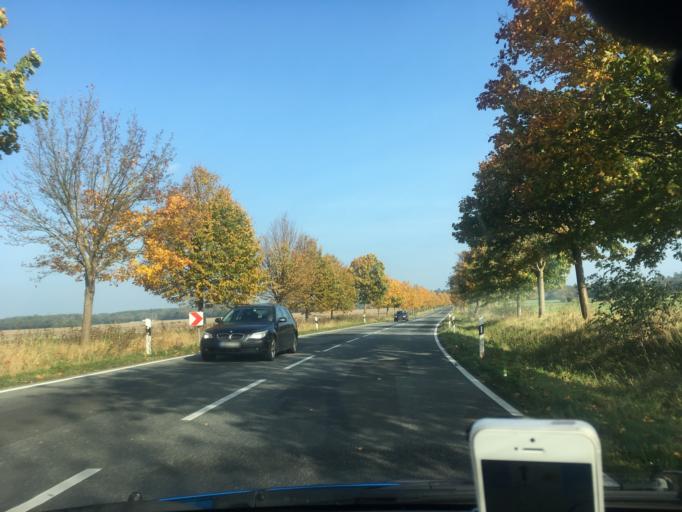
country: DE
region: Mecklenburg-Vorpommern
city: Stralendorf
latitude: 53.5396
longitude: 11.3064
